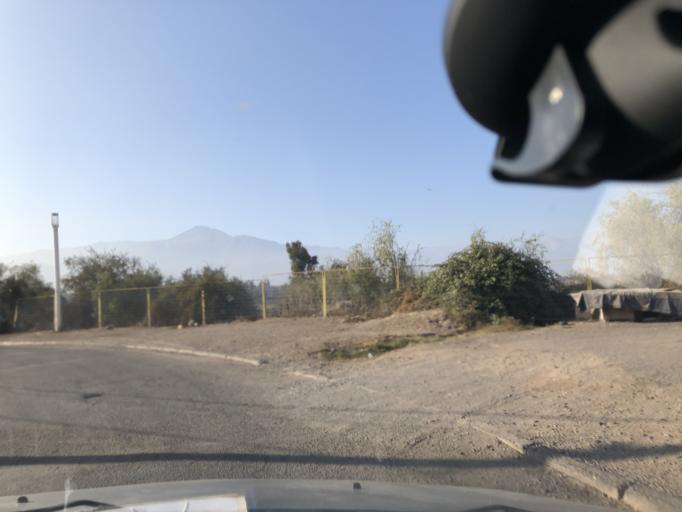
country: CL
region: Santiago Metropolitan
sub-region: Provincia de Cordillera
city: Puente Alto
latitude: -33.6291
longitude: -70.5845
